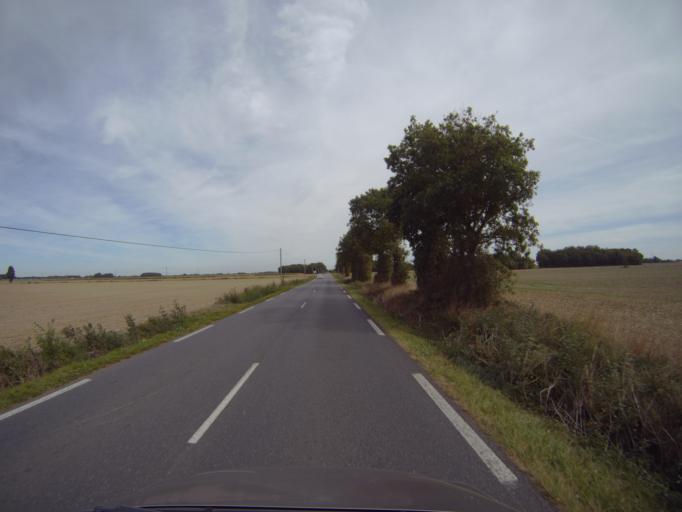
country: FR
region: Pays de la Loire
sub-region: Departement de la Vendee
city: Bouffere
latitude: 46.9733
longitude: -1.3816
